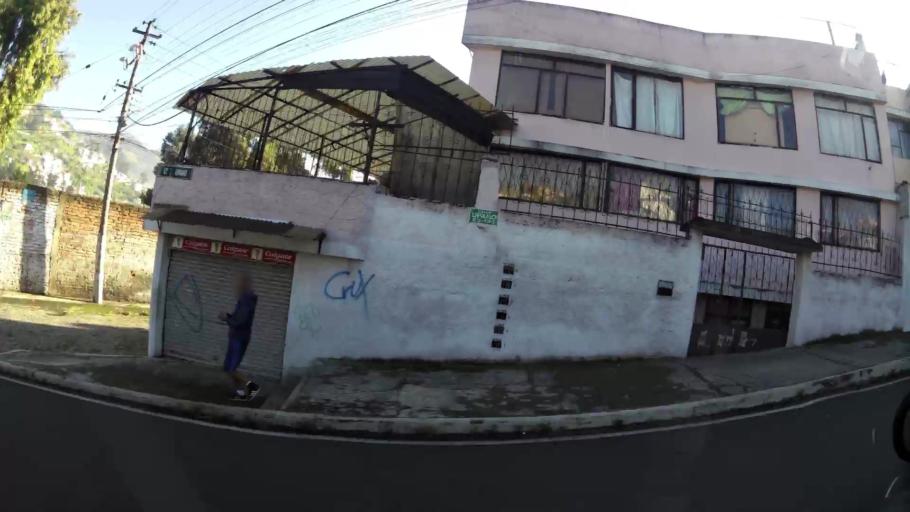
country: EC
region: Pichincha
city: Quito
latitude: -0.2358
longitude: -78.5126
